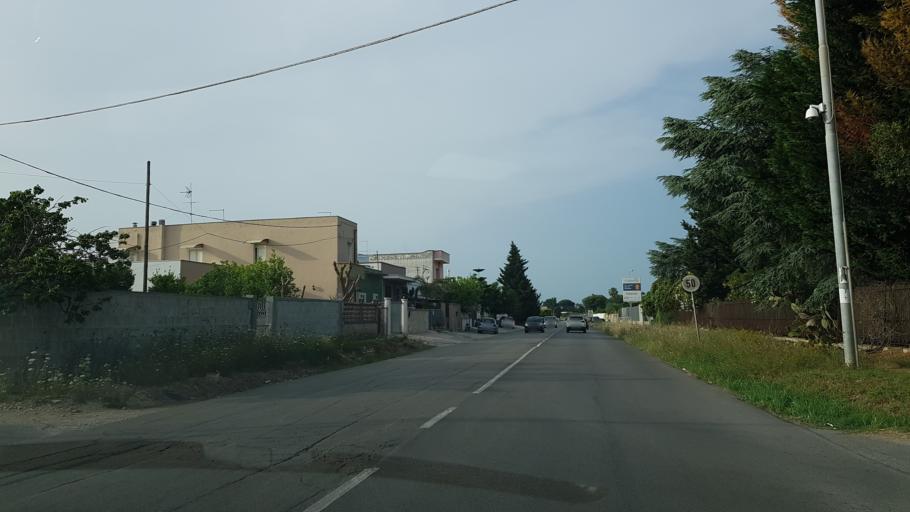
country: IT
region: Apulia
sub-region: Provincia di Brindisi
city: San Pietro Vernotico
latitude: 40.4946
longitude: 17.9909
